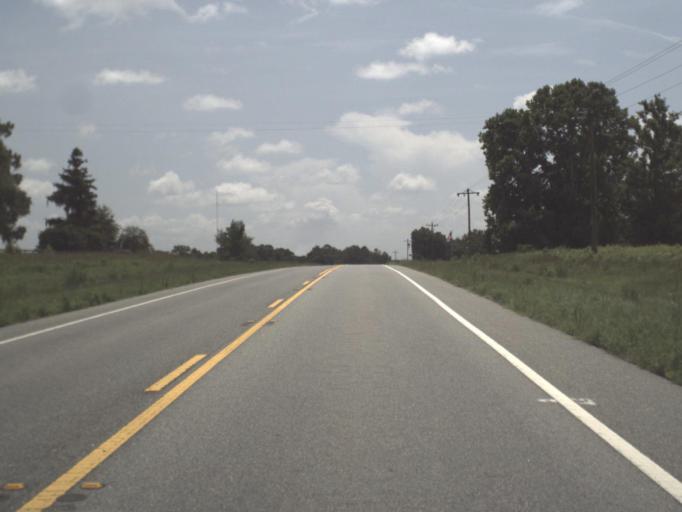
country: US
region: Florida
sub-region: Madison County
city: Madison
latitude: 30.4887
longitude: -83.4671
